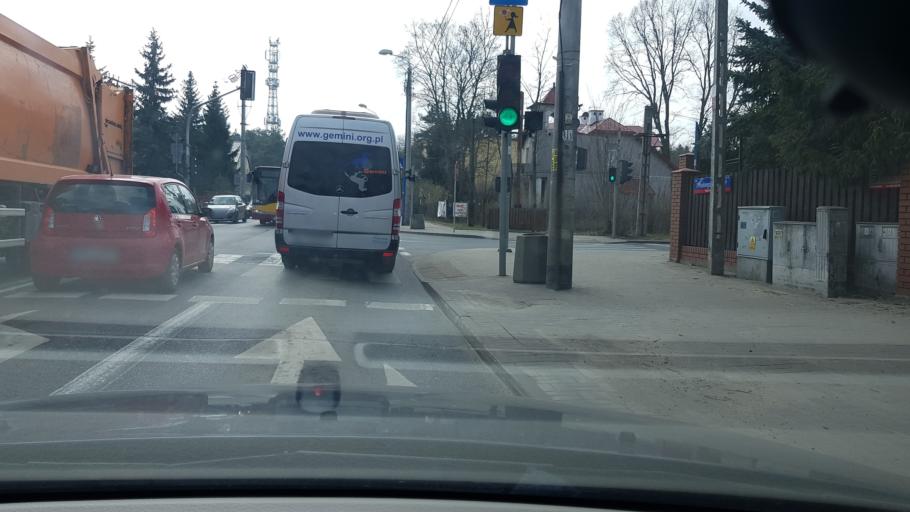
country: PL
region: Masovian Voivodeship
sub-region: Warszawa
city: Wesola
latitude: 52.2509
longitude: 21.2238
